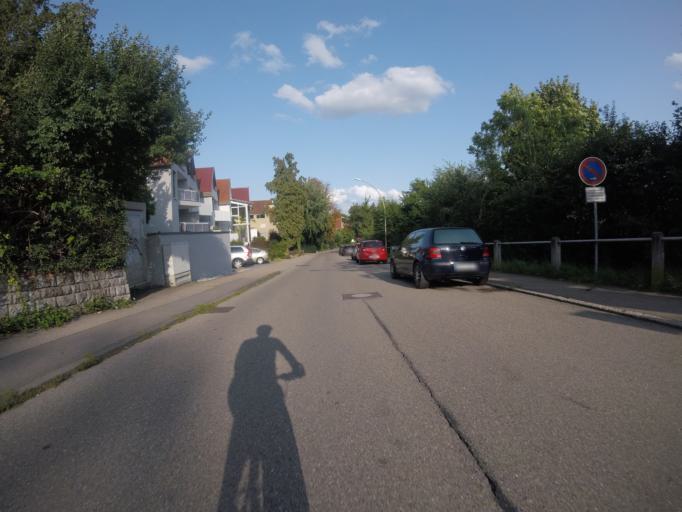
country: DE
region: Baden-Wuerttemberg
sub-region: Regierungsbezirk Stuttgart
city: Backnang
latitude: 48.9476
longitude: 9.4195
